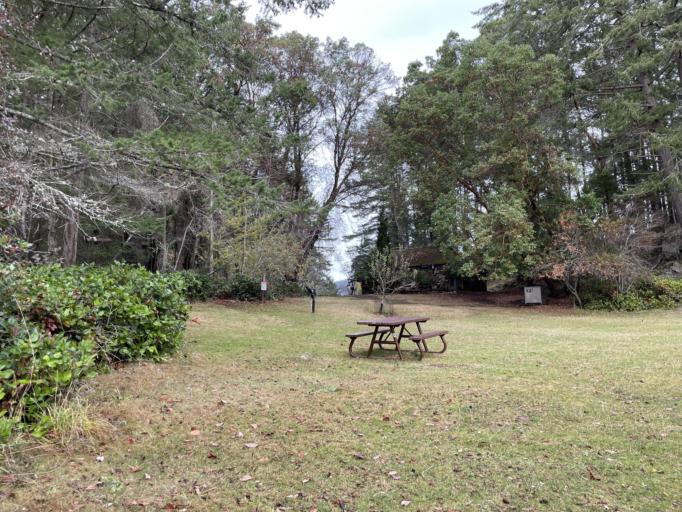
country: CA
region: British Columbia
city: North Cowichan
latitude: 48.9376
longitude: -123.5442
